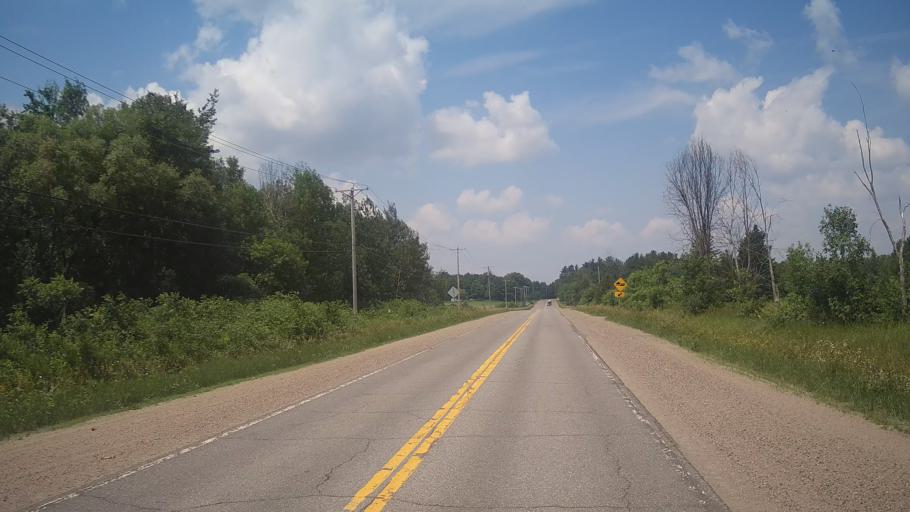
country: CA
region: Quebec
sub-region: Outaouais
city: Shawville
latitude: 45.5717
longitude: -76.4388
